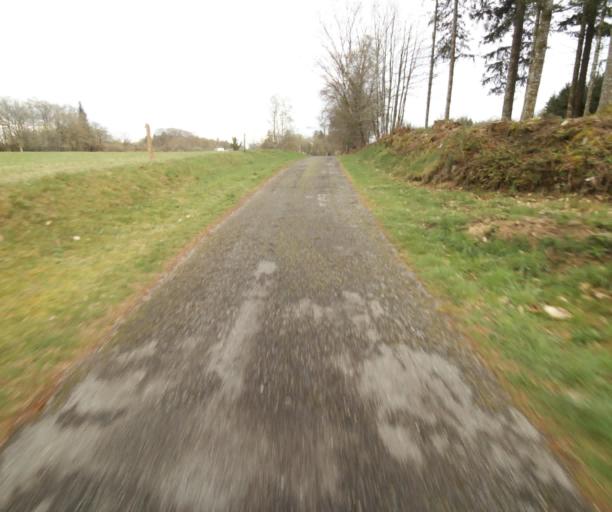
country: FR
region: Limousin
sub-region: Departement de la Correze
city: Saint-Privat
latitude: 45.2197
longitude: 2.0138
